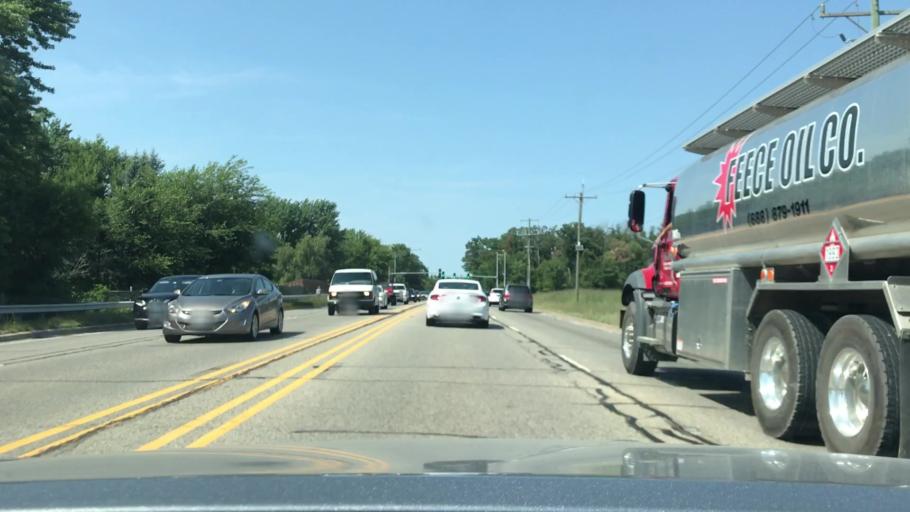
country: US
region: Illinois
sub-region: Kane County
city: Batavia
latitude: 41.8388
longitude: -88.2795
